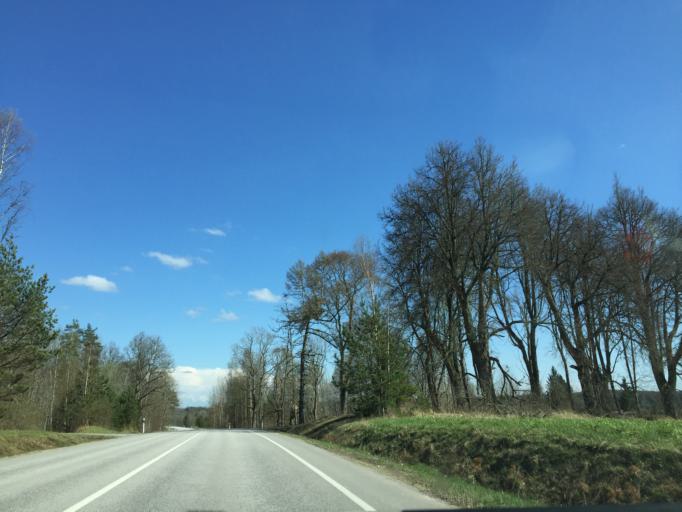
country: EE
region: Valgamaa
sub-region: Valga linn
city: Valga
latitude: 57.8543
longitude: 26.1430
